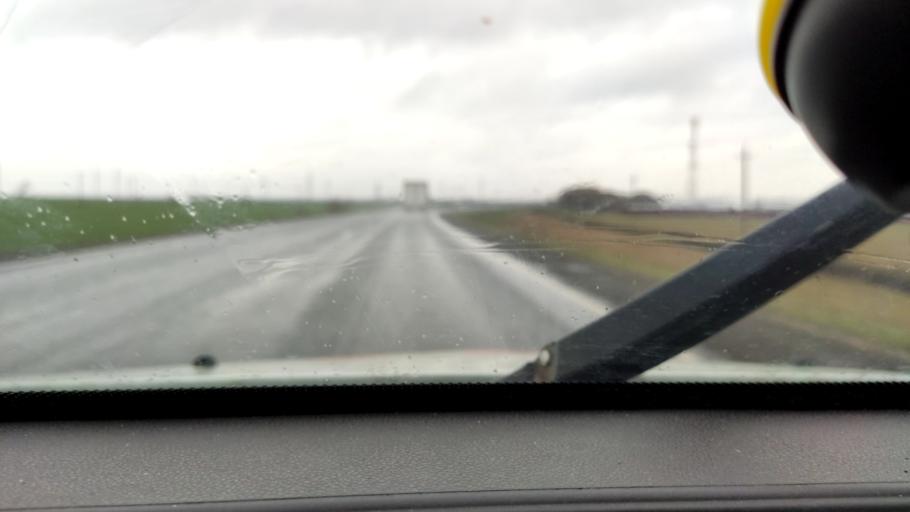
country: RU
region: Samara
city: Povolzhskiy
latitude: 53.6363
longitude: 49.6586
